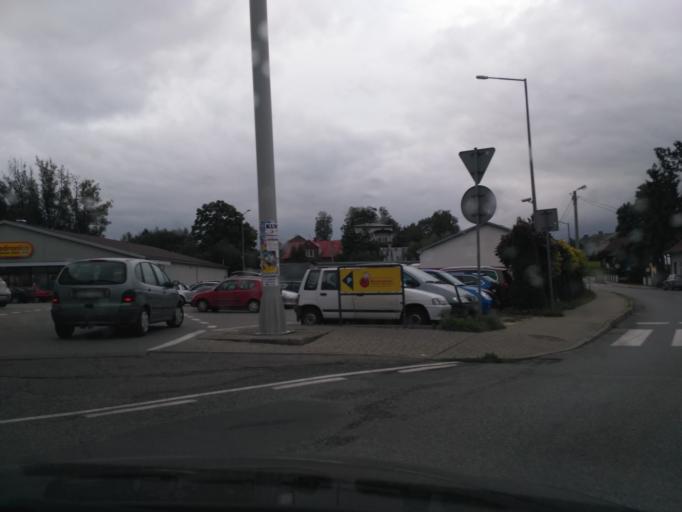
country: PL
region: Subcarpathian Voivodeship
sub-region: Powiat krosnienski
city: Korczyna
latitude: 49.7141
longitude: 21.8113
